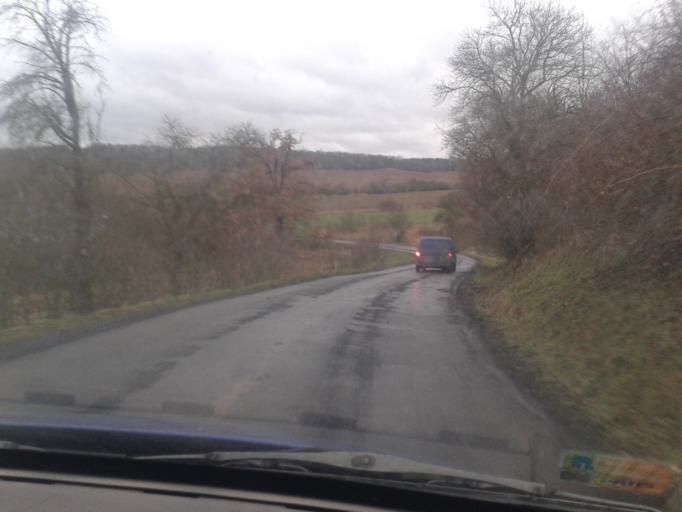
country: CZ
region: Central Bohemia
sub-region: Okres Beroun
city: Beroun
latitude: 49.8958
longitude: 14.1404
